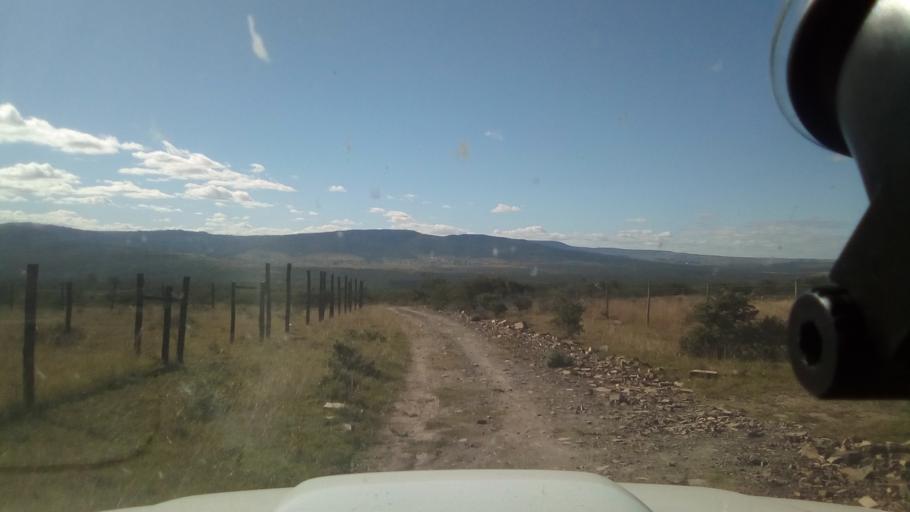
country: ZA
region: Eastern Cape
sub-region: Buffalo City Metropolitan Municipality
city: Bhisho
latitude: -32.7787
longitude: 27.3363
